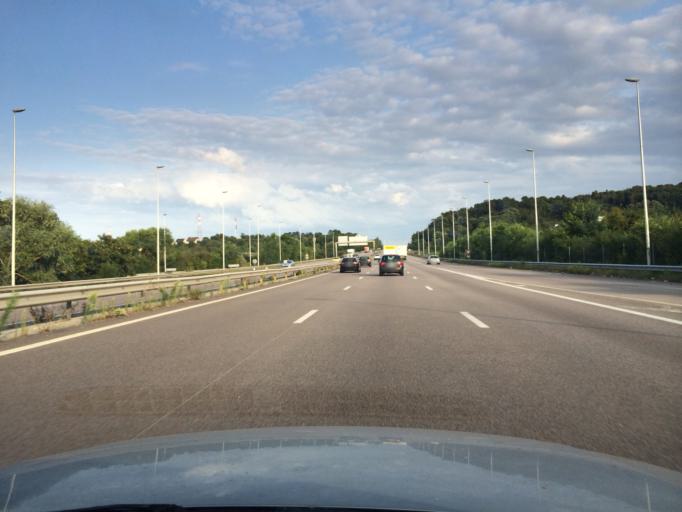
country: FR
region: Haute-Normandie
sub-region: Departement de la Seine-Maritime
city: Oissel
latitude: 49.3268
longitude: 1.0919
